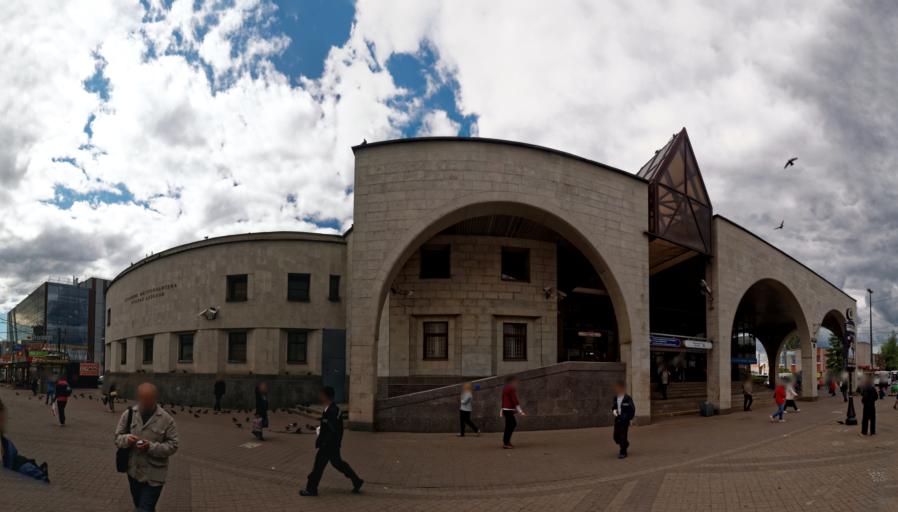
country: RU
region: St.-Petersburg
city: Staraya Derevnya
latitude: 59.9895
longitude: 30.2557
